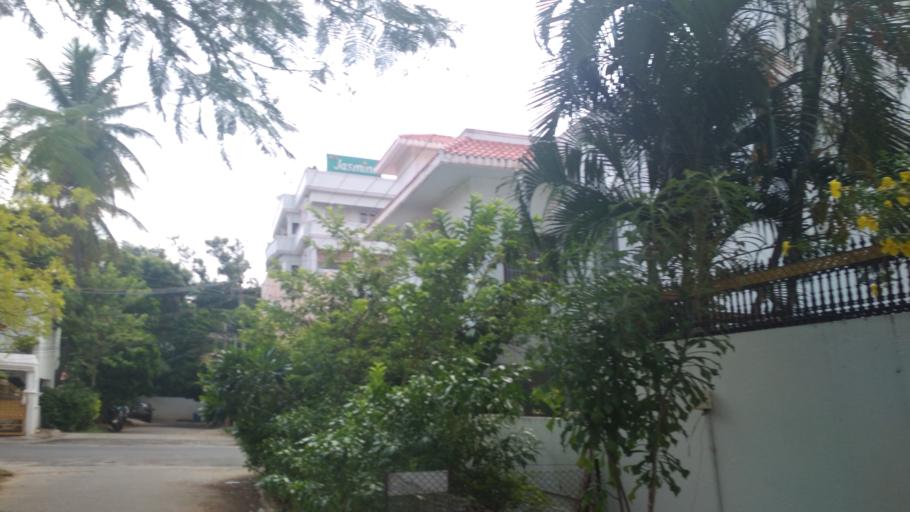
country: IN
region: Tamil Nadu
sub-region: Coimbatore
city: Coimbatore
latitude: 11.0248
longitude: 76.9384
